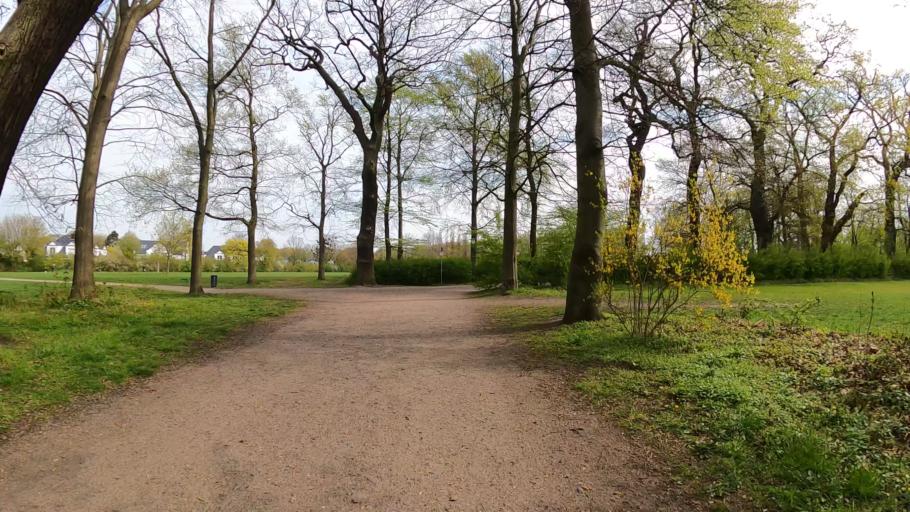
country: DE
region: Hamburg
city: Eidelstedt
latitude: 53.5543
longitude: 9.8595
